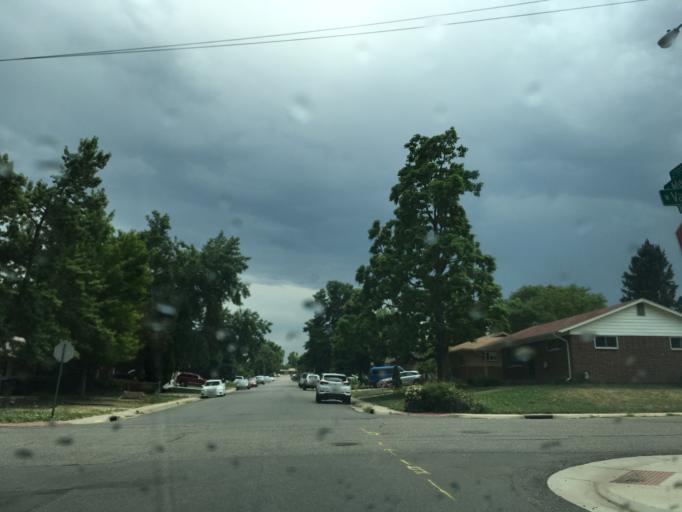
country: US
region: Colorado
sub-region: Arapahoe County
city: Sheridan
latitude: 39.6705
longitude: -105.0360
